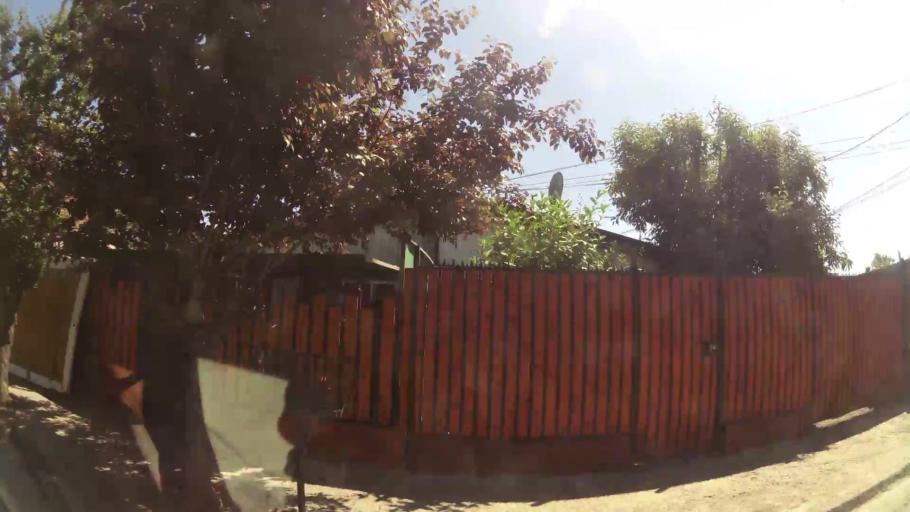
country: CL
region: Santiago Metropolitan
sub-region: Provincia de Maipo
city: San Bernardo
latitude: -33.6276
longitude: -70.6982
